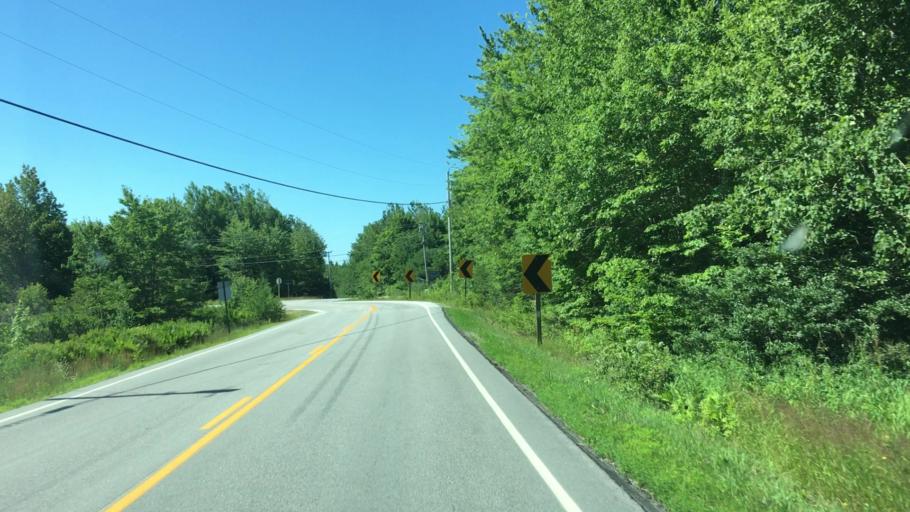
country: US
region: Maine
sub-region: Hancock County
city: Penobscot
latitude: 44.4640
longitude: -68.6370
